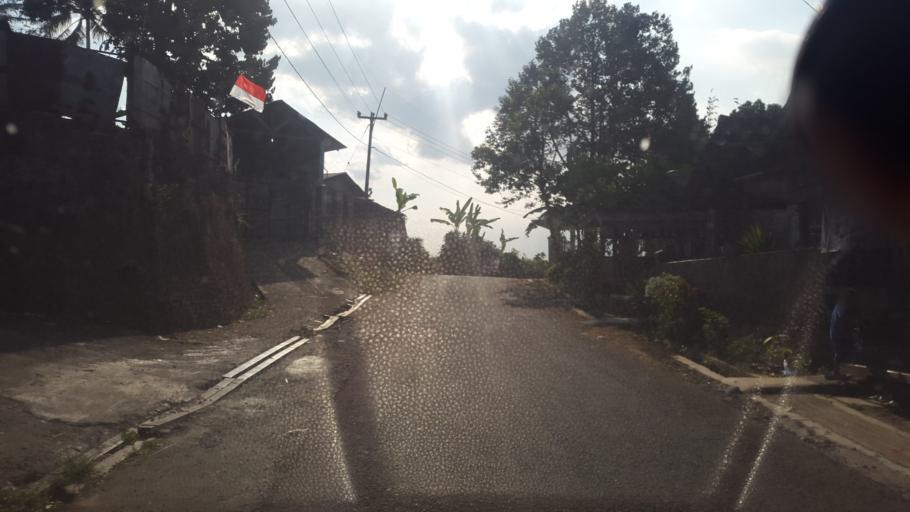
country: ID
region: West Java
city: Cicurug
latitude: -6.8614
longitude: 106.7518
